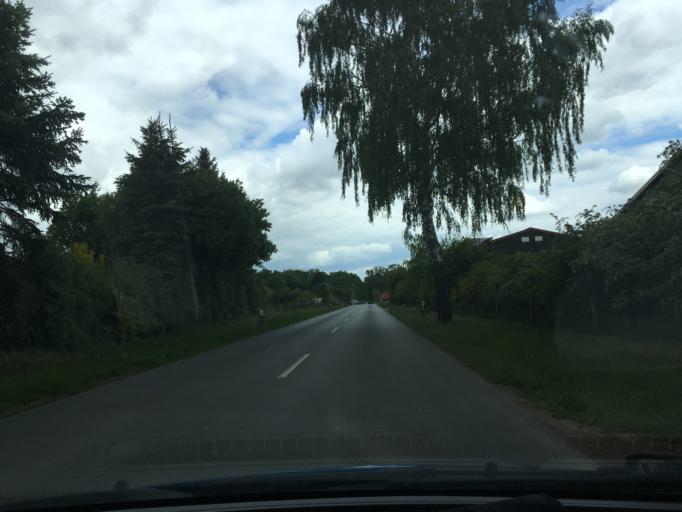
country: DE
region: Lower Saxony
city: Suderburg
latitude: 52.9195
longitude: 10.5098
